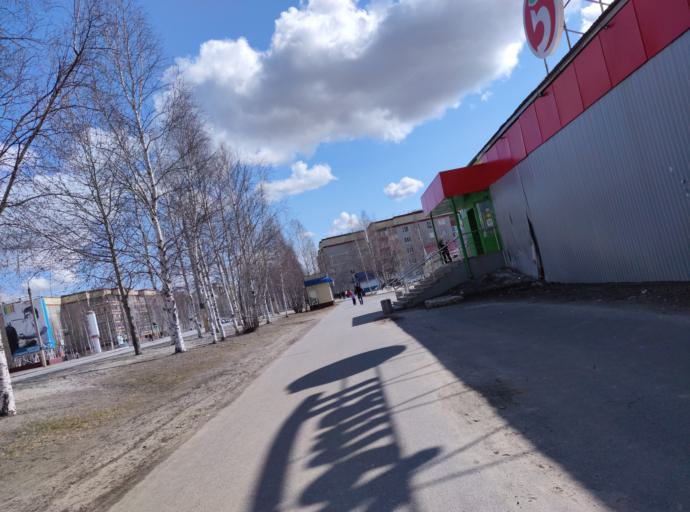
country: RU
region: Khanty-Mansiyskiy Avtonomnyy Okrug
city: Langepas
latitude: 61.2525
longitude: 75.1737
